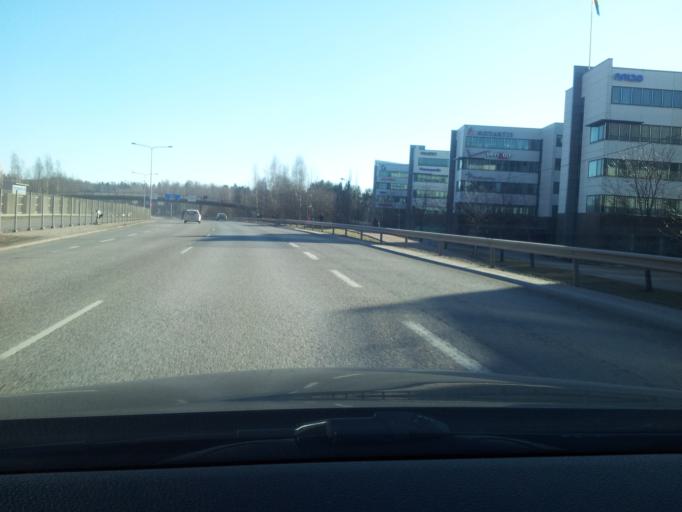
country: FI
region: Uusimaa
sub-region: Helsinki
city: Otaniemi
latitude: 60.1884
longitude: 24.8073
